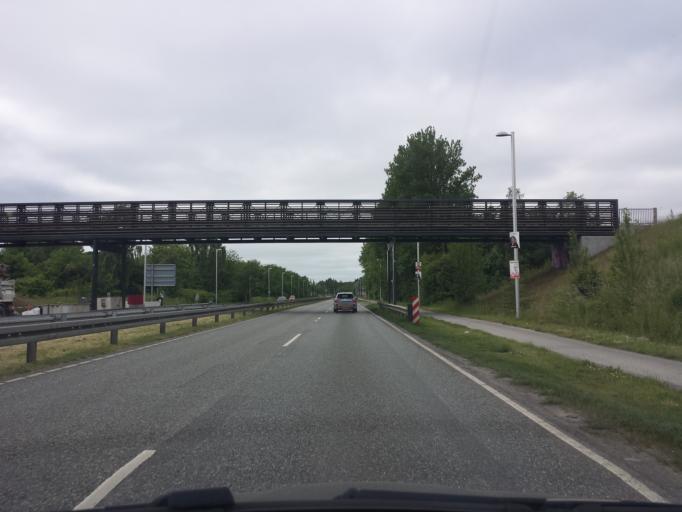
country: DK
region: Capital Region
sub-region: Glostrup Kommune
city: Glostrup
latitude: 55.6897
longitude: 12.4045
